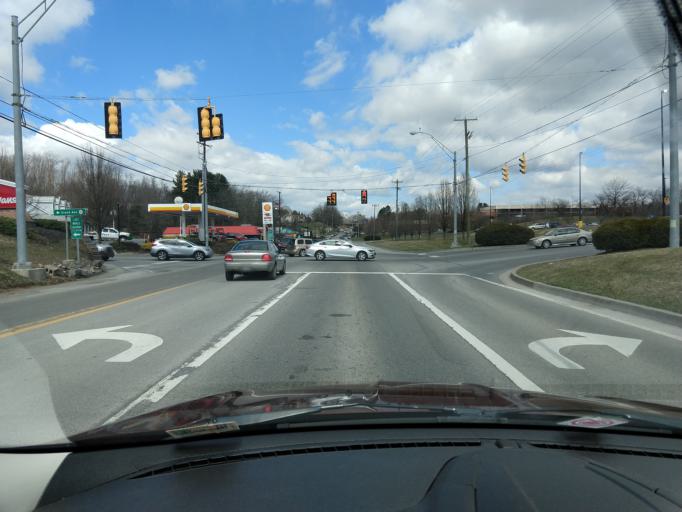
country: US
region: West Virginia
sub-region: Greenbrier County
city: Lewisburg
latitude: 37.8121
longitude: -80.4321
